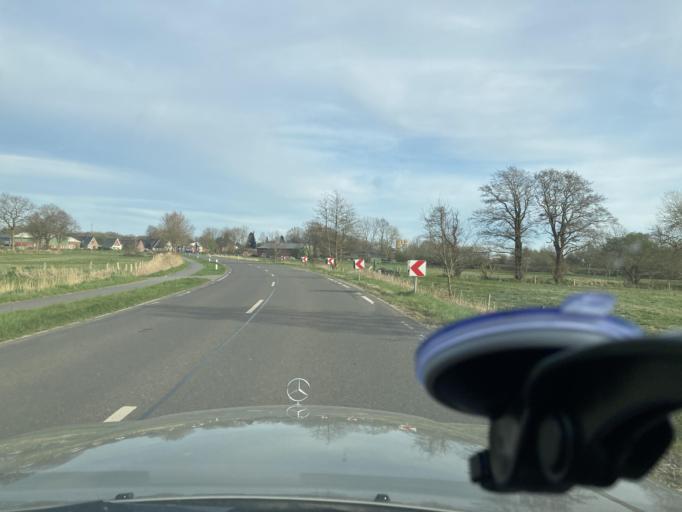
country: DE
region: Schleswig-Holstein
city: Weddingstedt
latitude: 54.2415
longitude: 9.0796
